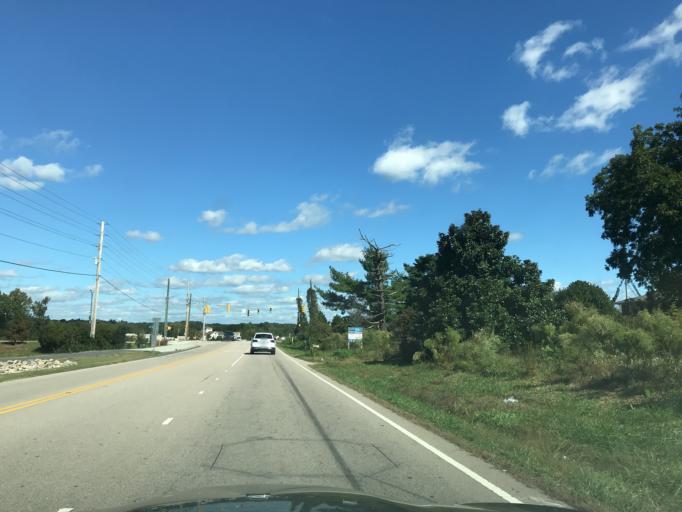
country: US
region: North Carolina
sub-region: Wake County
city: Wake Forest
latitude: 35.9424
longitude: -78.5072
